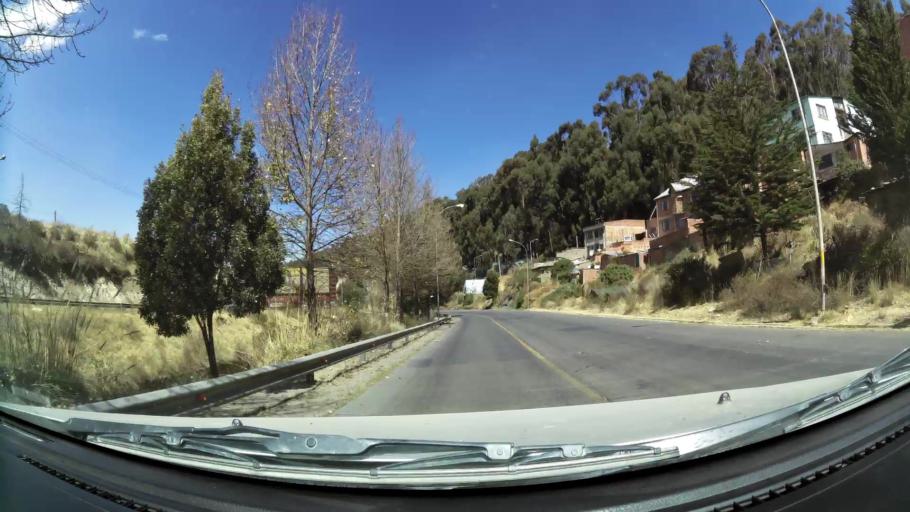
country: BO
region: La Paz
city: La Paz
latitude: -16.4745
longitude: -68.1534
